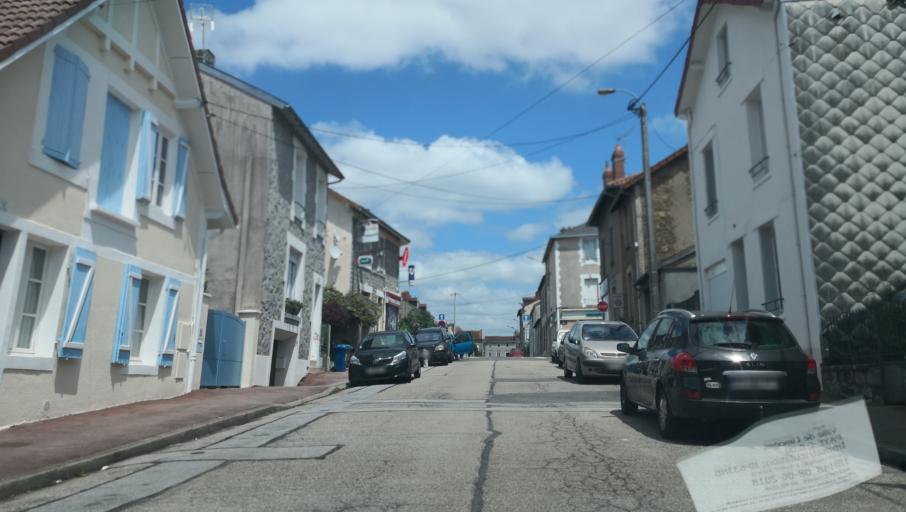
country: FR
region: Limousin
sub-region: Departement de la Haute-Vienne
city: Limoges
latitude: 45.8377
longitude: 1.2453
